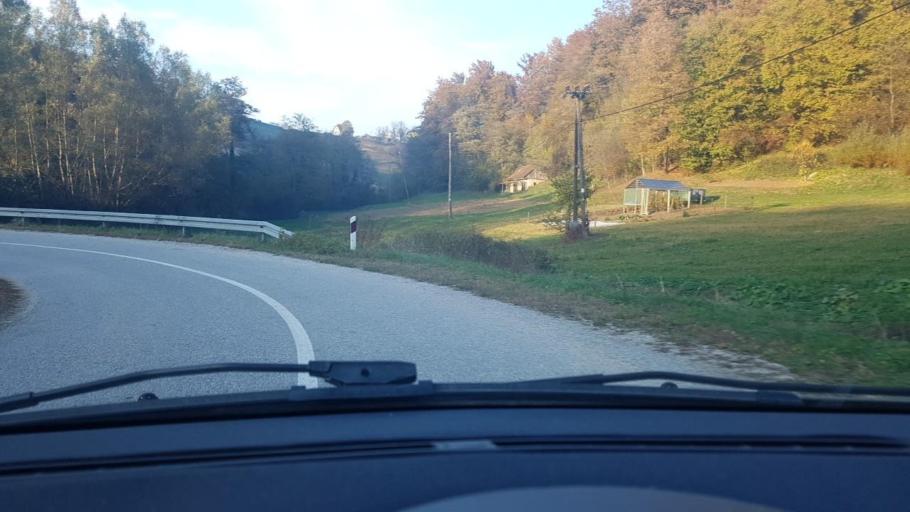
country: SI
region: Podcetrtek
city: Podcetrtek
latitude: 46.1807
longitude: 15.6444
